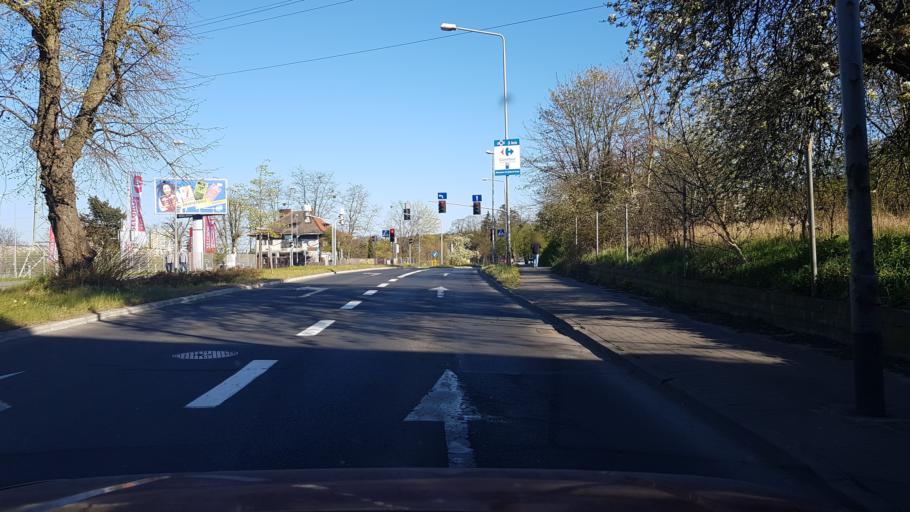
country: PL
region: West Pomeranian Voivodeship
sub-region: Szczecin
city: Szczecin
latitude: 53.3783
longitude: 14.6382
